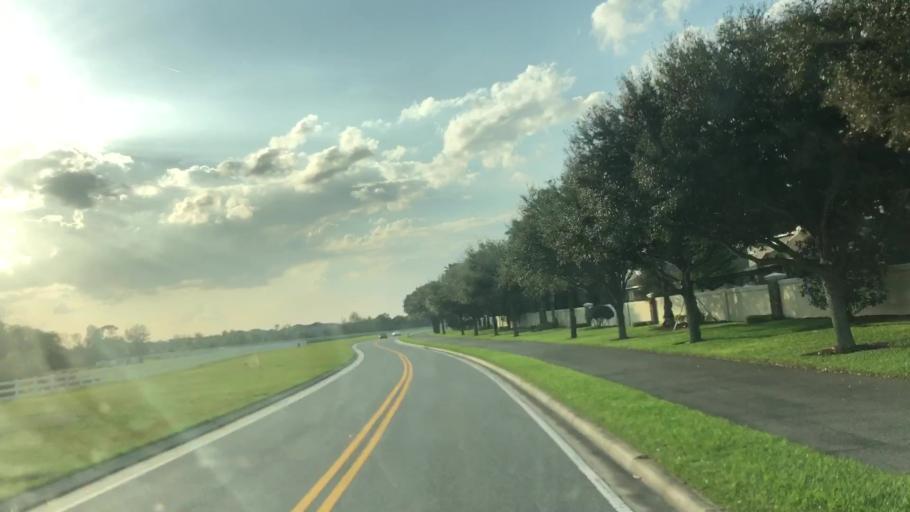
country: US
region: Florida
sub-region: Orange County
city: Lake Butler
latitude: 28.4463
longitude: -81.6066
